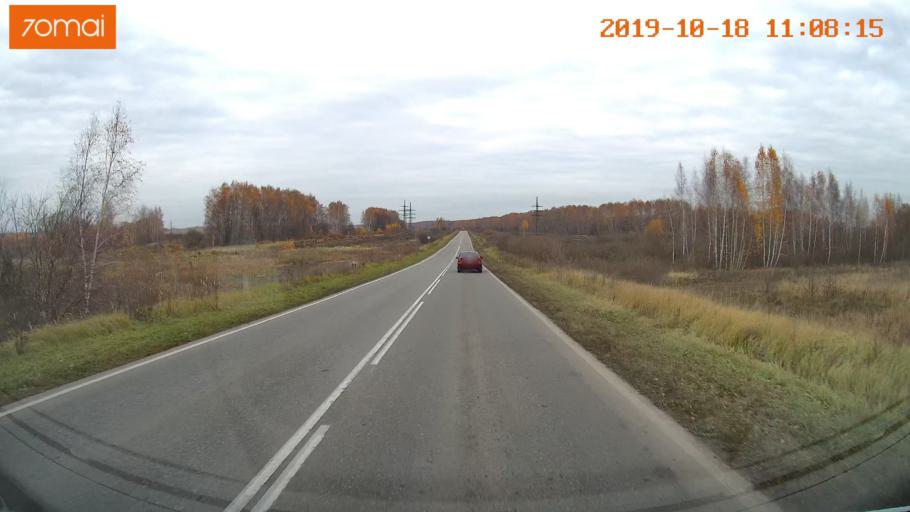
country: RU
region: Tula
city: Kimovsk
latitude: 53.9351
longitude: 38.5382
